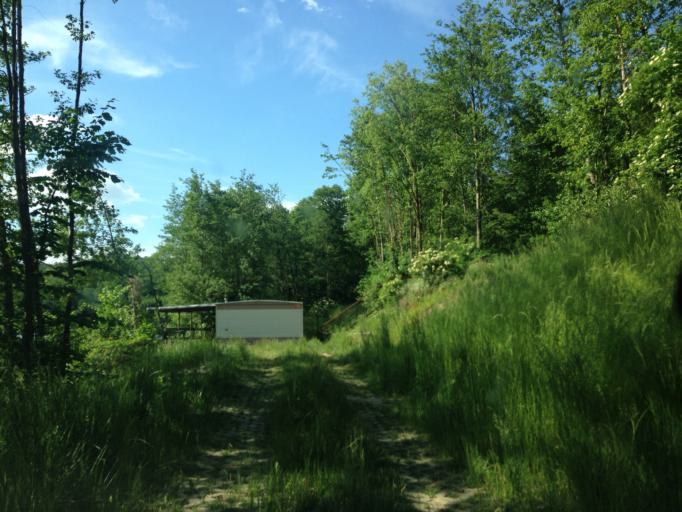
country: PL
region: Kujawsko-Pomorskie
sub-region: Powiat brodnicki
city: Brzozie
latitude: 53.3174
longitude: 19.5671
